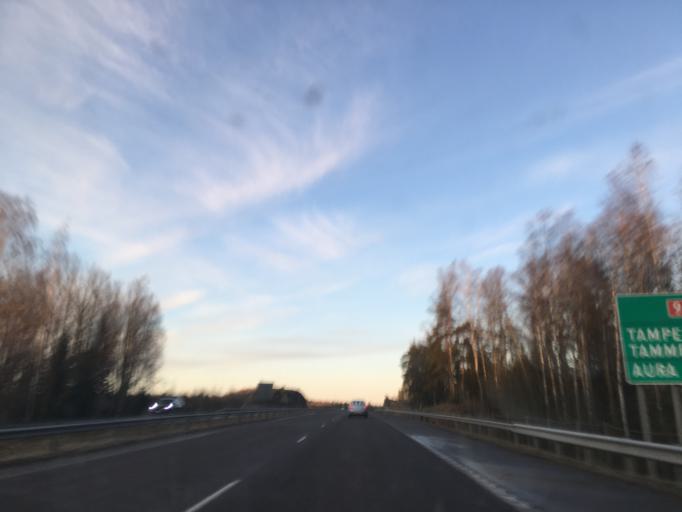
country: FI
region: Varsinais-Suomi
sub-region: Turku
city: Turku
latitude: 60.5122
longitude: 22.3021
